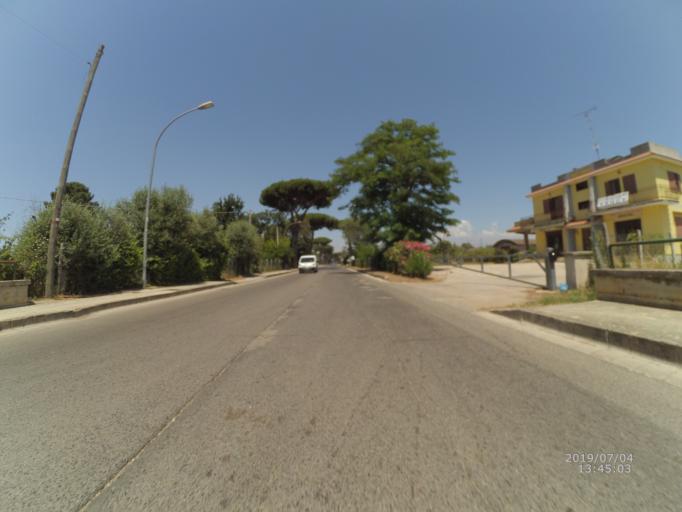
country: IT
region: Latium
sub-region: Provincia di Latina
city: San Felice Circeo
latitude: 41.2601
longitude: 13.0918
